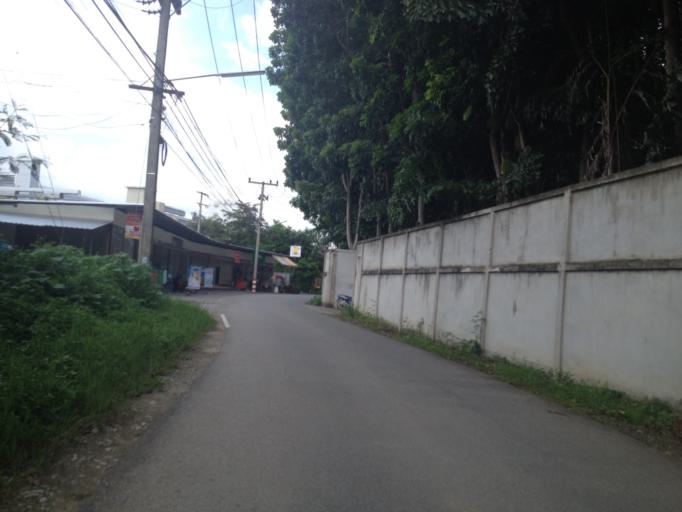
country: TH
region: Chiang Mai
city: Hang Dong
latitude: 18.7150
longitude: 98.9333
